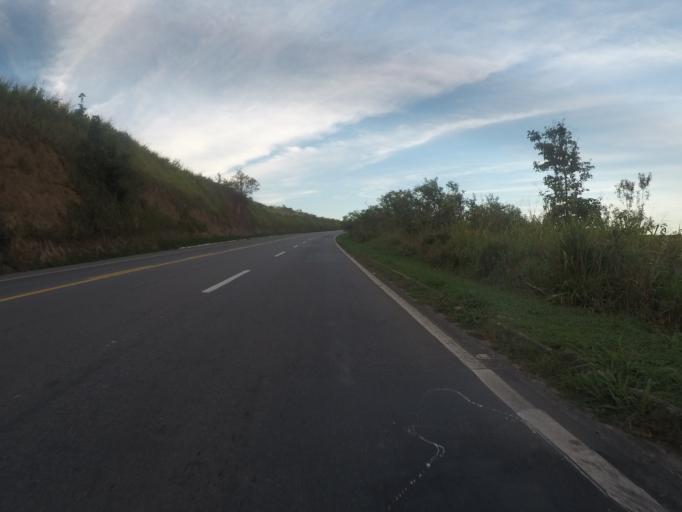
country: BR
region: Espirito Santo
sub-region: Aracruz
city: Aracruz
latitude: -19.6656
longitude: -40.2507
